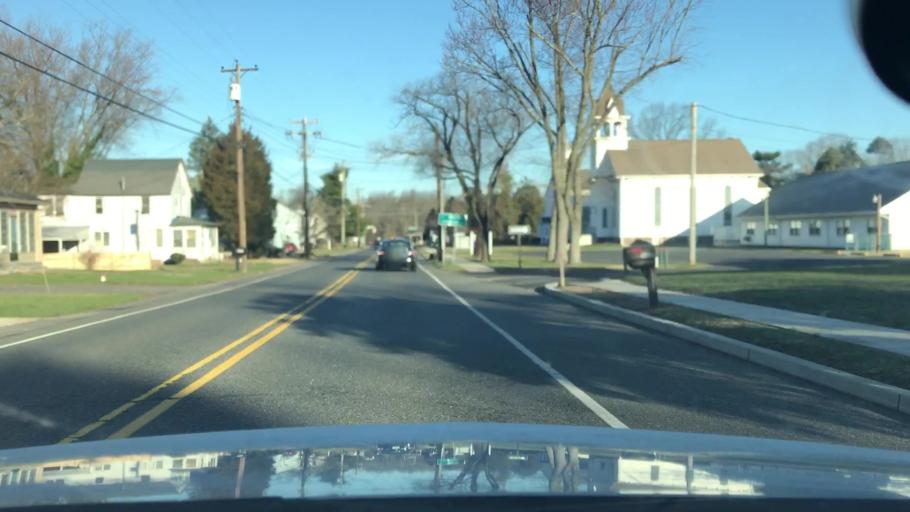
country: US
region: New Jersey
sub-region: Gloucester County
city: Williamstown
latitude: 39.7115
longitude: -75.0275
